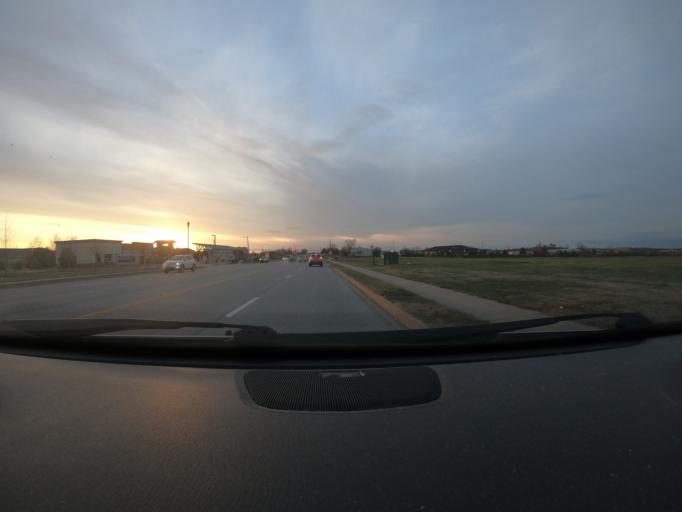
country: US
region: Arkansas
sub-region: Benton County
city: Bentonville
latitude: 36.3358
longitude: -94.2180
